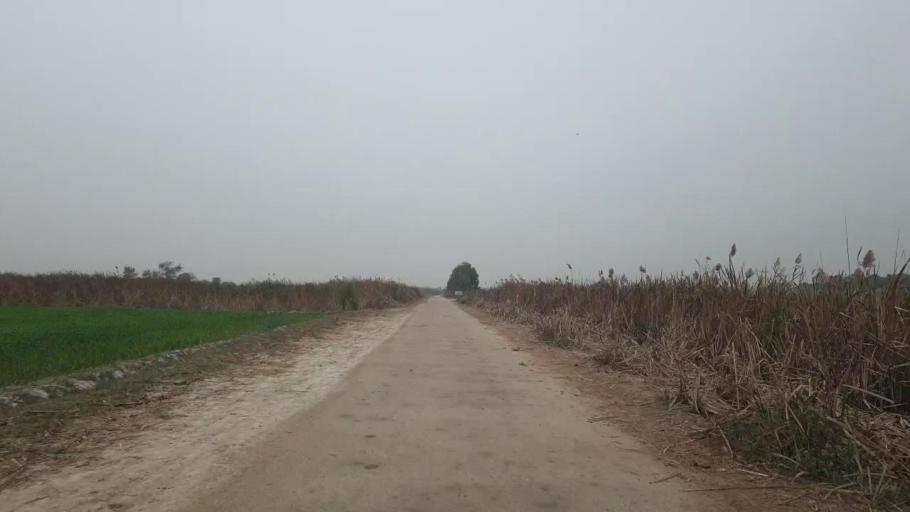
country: PK
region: Sindh
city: Tando Adam
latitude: 25.8387
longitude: 68.6573
